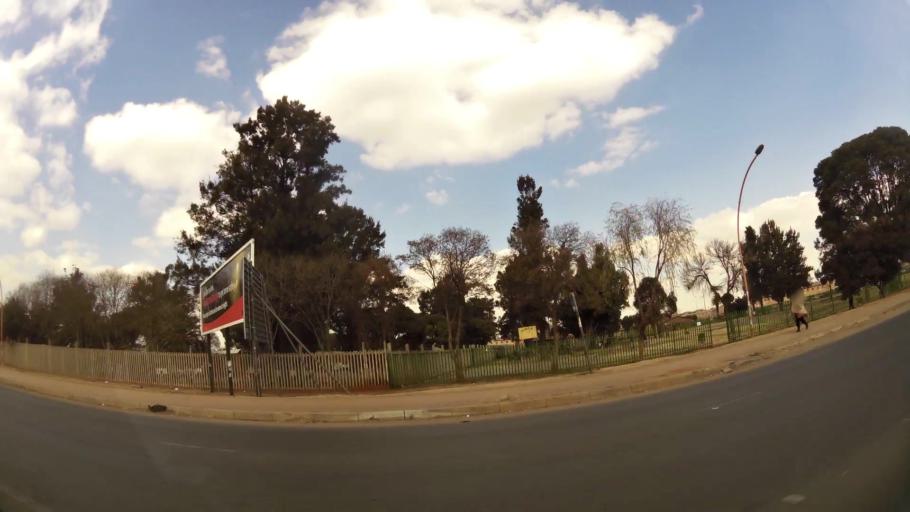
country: ZA
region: Gauteng
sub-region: Ekurhuleni Metropolitan Municipality
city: Tembisa
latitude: -25.9973
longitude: 28.2431
